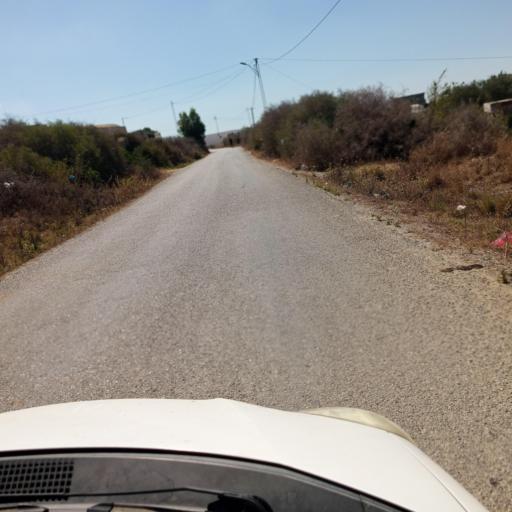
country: TN
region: Nabul
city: Qulaybiyah
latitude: 36.8649
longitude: 11.0337
